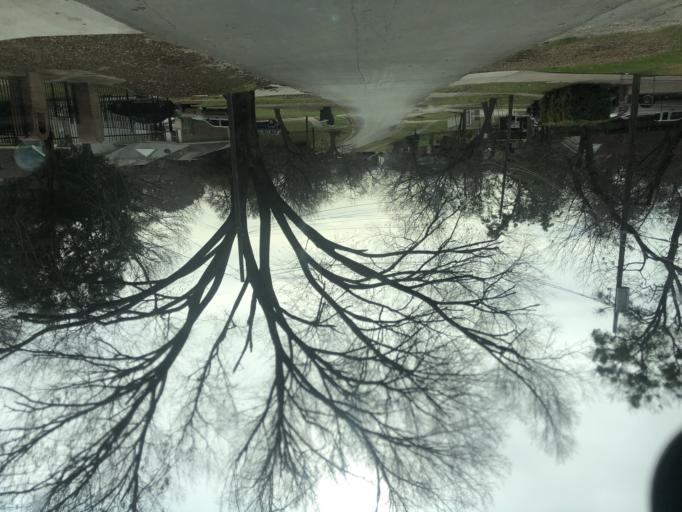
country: US
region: Texas
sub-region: Dallas County
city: Duncanville
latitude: 32.6673
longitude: -96.8337
